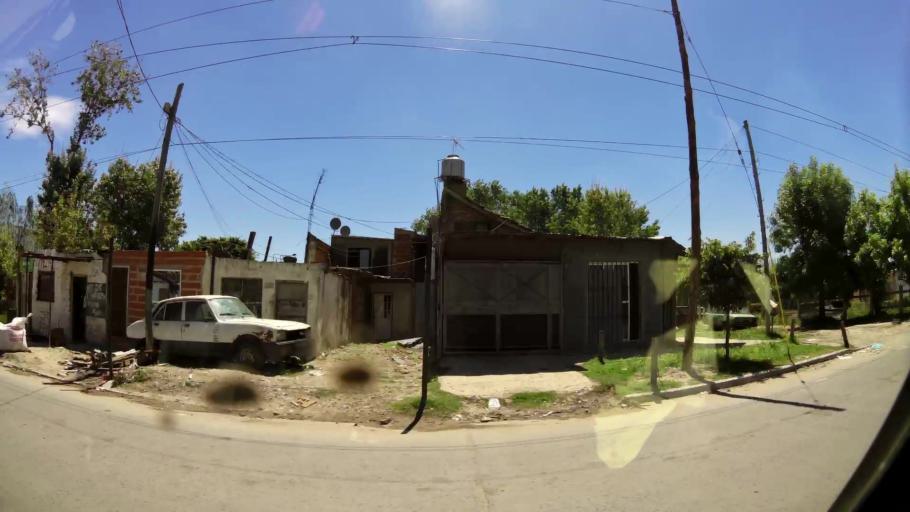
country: AR
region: Buenos Aires
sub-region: Partido de Quilmes
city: Quilmes
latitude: -34.7246
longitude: -58.3147
